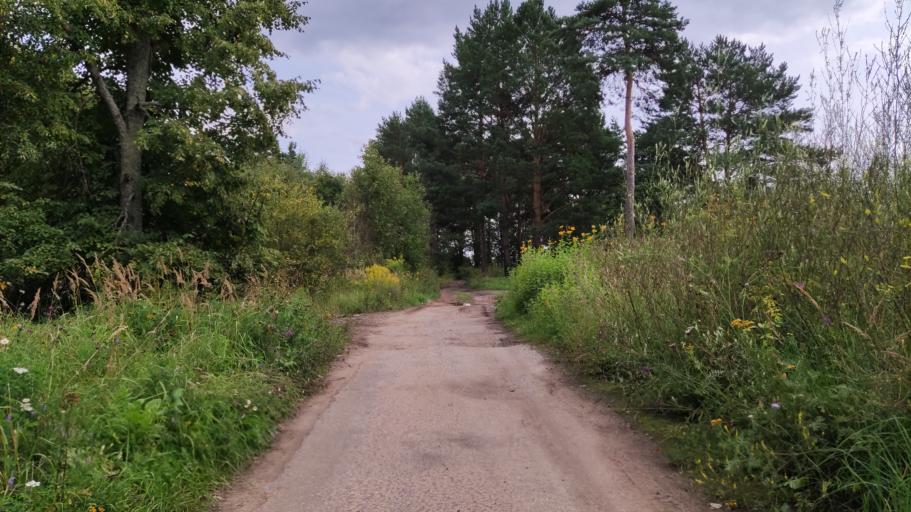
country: RU
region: Tverskaya
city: Rzhev
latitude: 56.2437
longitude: 34.3743
